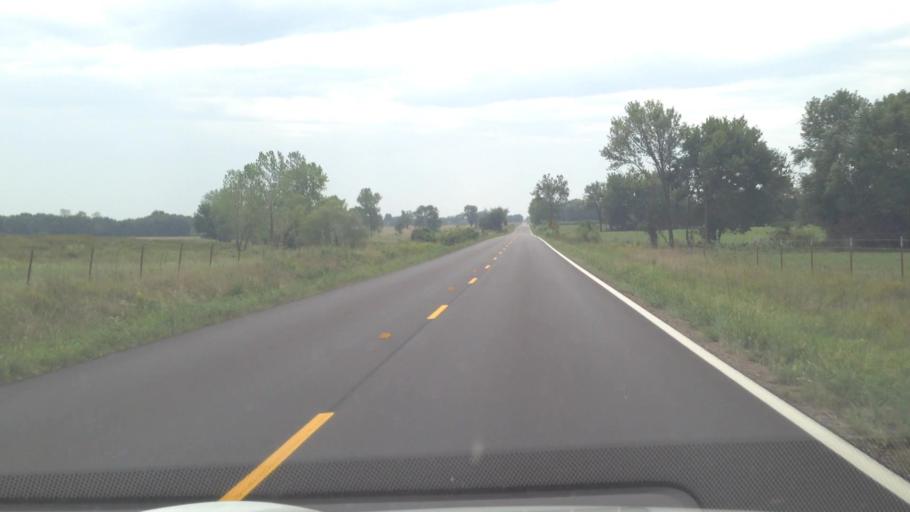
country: US
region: Kansas
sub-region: Crawford County
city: Girard
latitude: 37.5425
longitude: -94.9605
